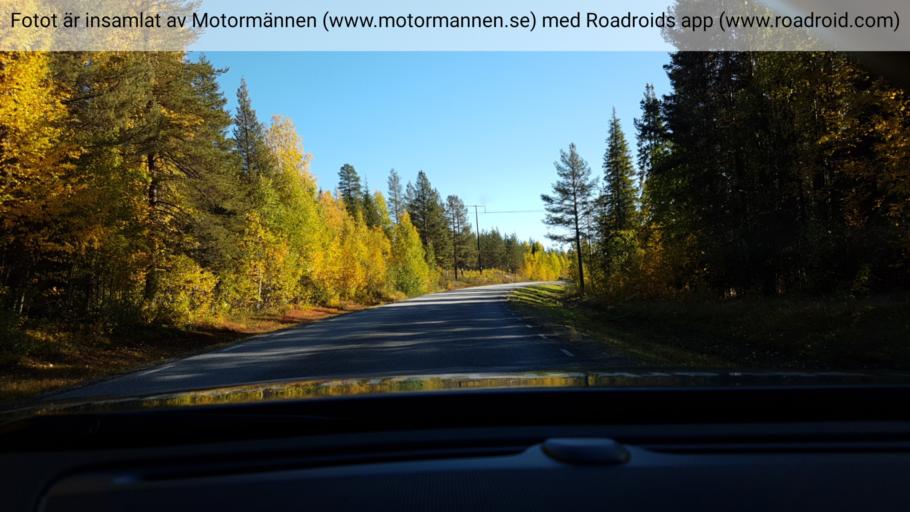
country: SE
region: Norrbotten
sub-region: Gallivare Kommun
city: Gaellivare
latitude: 66.4532
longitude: 20.7102
